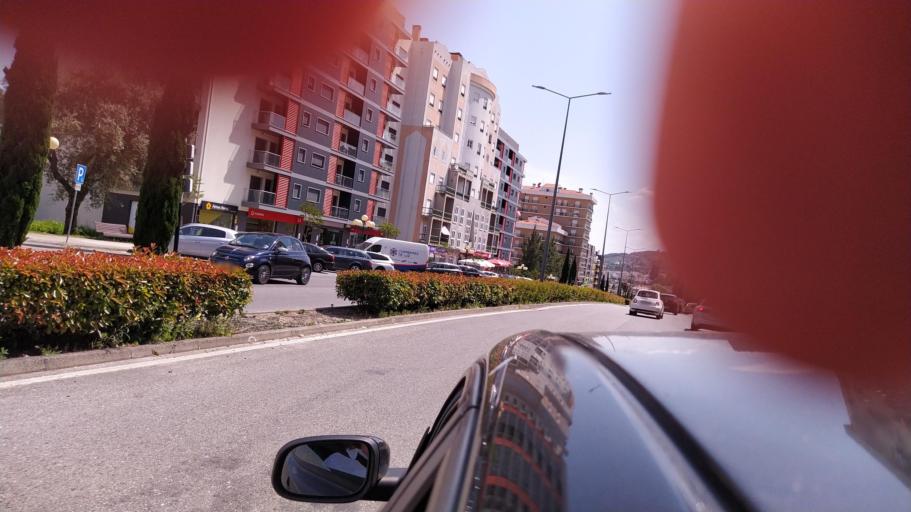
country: PT
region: Castelo Branco
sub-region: Covilha
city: Covilha
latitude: 40.2732
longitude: -7.4993
